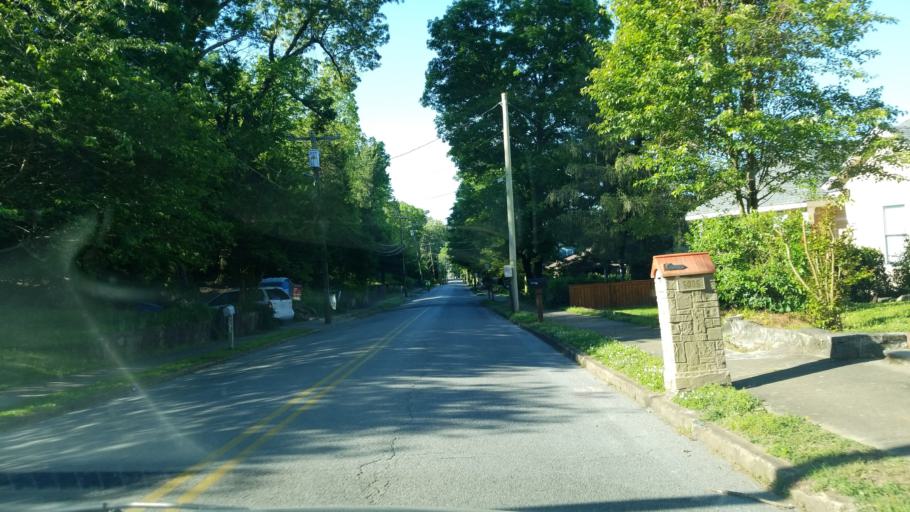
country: US
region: Tennessee
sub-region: Hamilton County
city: Lookout Mountain
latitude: 34.9931
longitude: -85.3265
